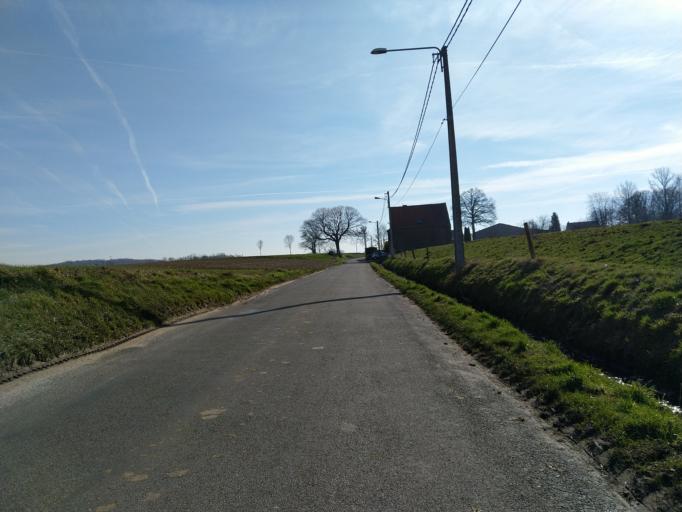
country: BE
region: Wallonia
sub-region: Province du Hainaut
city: Jurbise
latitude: 50.5304
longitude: 3.9482
